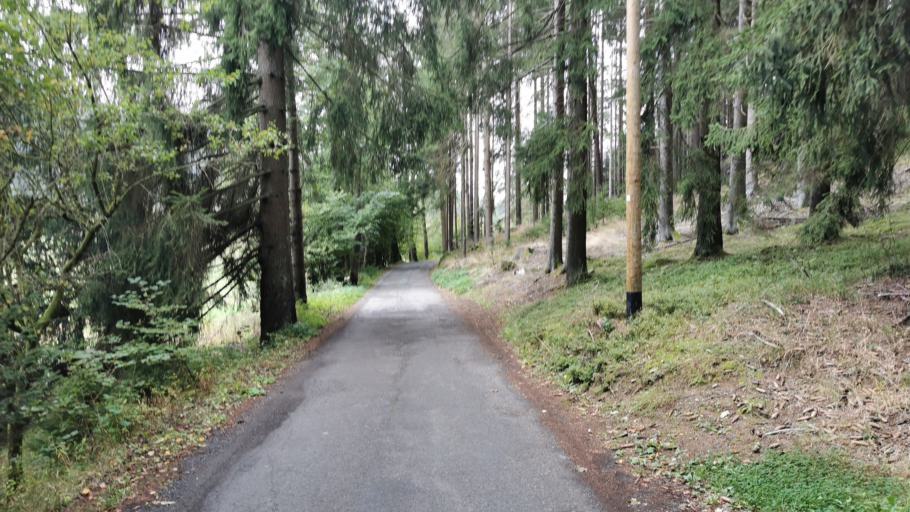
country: DE
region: Bavaria
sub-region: Upper Franconia
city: Teuschnitz
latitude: 50.4240
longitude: 11.3802
